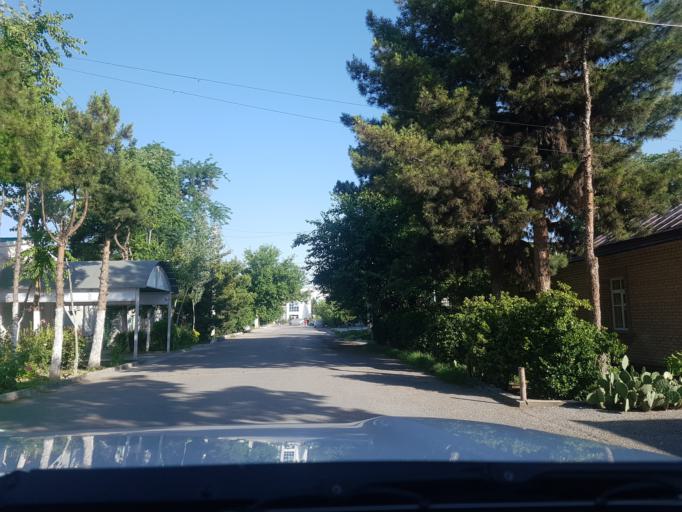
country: TM
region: Ahal
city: Ashgabat
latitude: 37.9541
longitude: 58.3581
